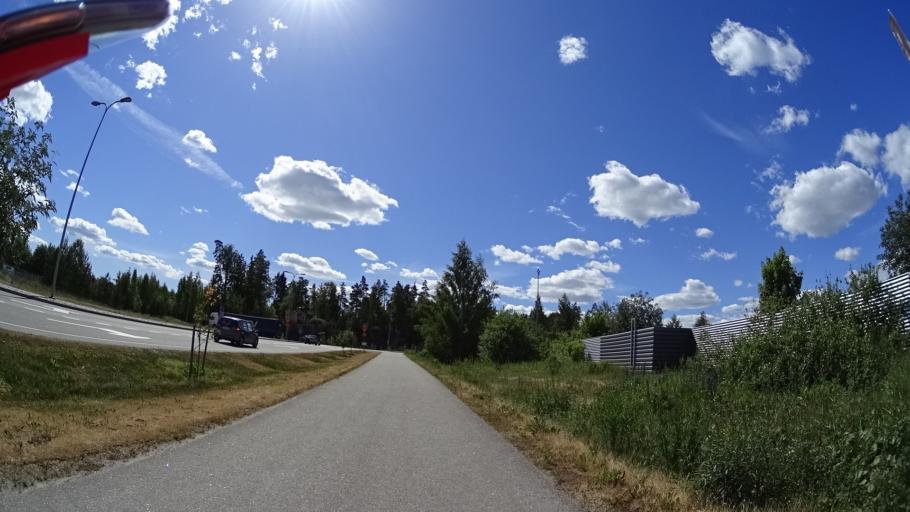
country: FI
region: Uusimaa
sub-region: Helsinki
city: Vantaa
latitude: 60.2955
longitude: 24.9165
